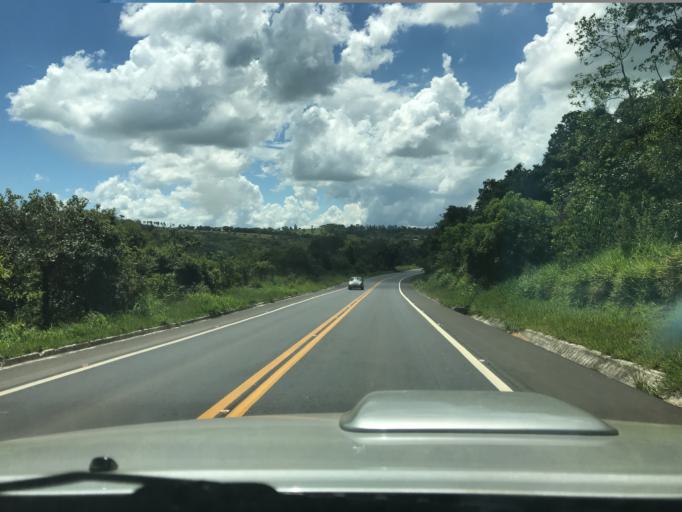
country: BR
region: Minas Gerais
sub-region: Formiga
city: Formiga
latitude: -20.6454
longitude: -45.3601
